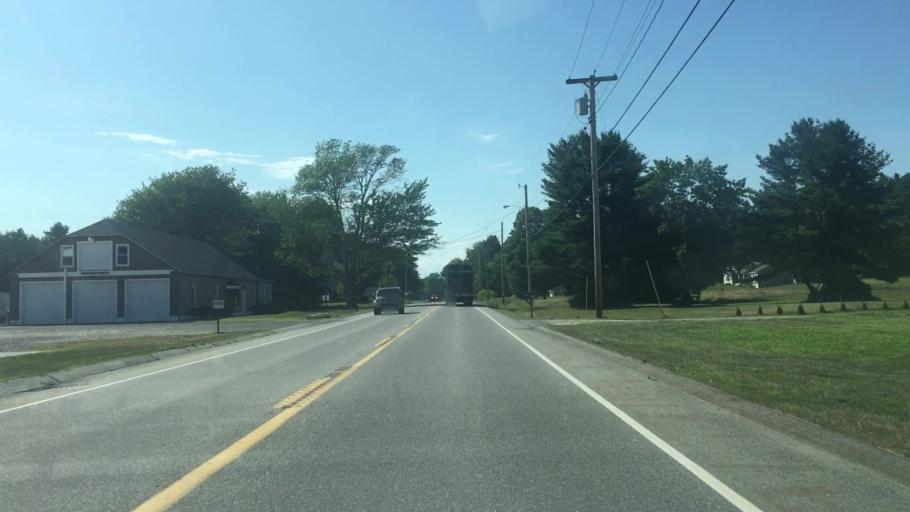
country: US
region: Maine
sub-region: York County
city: Buxton
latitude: 43.5673
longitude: -70.5048
